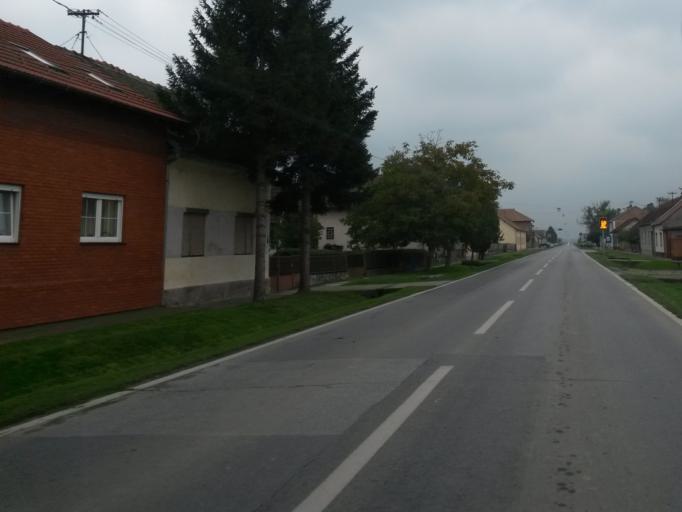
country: HR
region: Osjecko-Baranjska
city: Vuka
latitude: 45.4067
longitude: 18.4677
